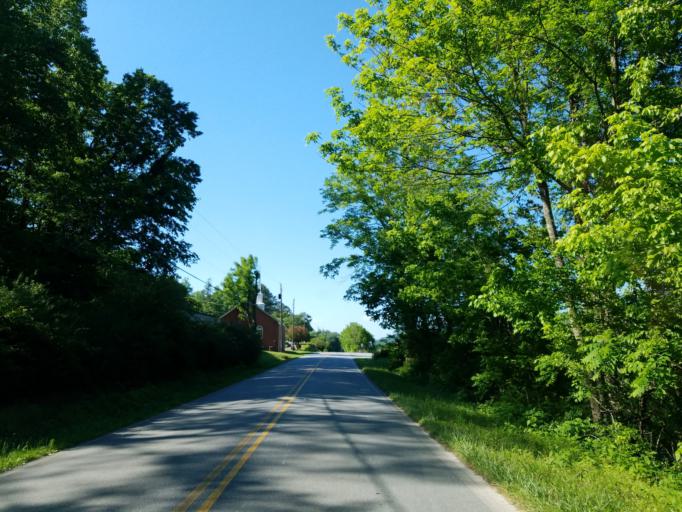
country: US
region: Georgia
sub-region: Pickens County
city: Jasper
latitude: 34.5619
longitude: -84.5116
